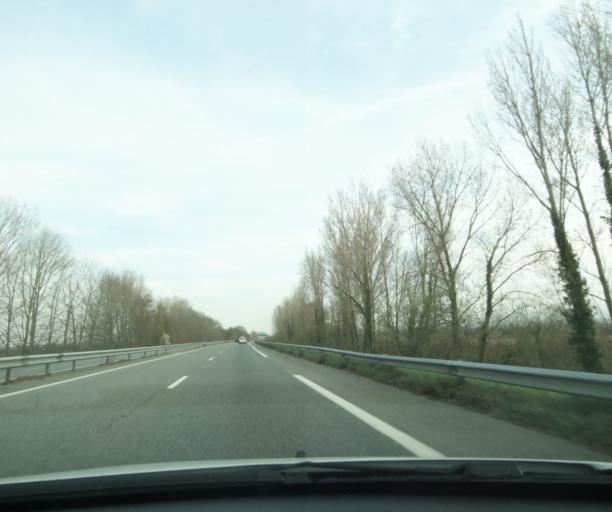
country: FR
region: Midi-Pyrenees
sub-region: Departement des Hautes-Pyrenees
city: Juillan
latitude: 43.2166
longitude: 0.0257
